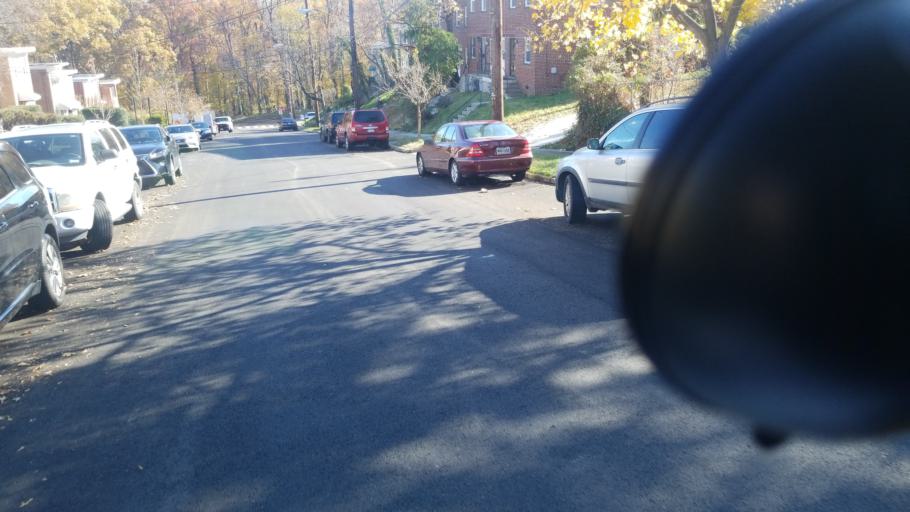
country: US
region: Maryland
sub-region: Prince George's County
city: Coral Hills
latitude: 38.8838
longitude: -76.9469
